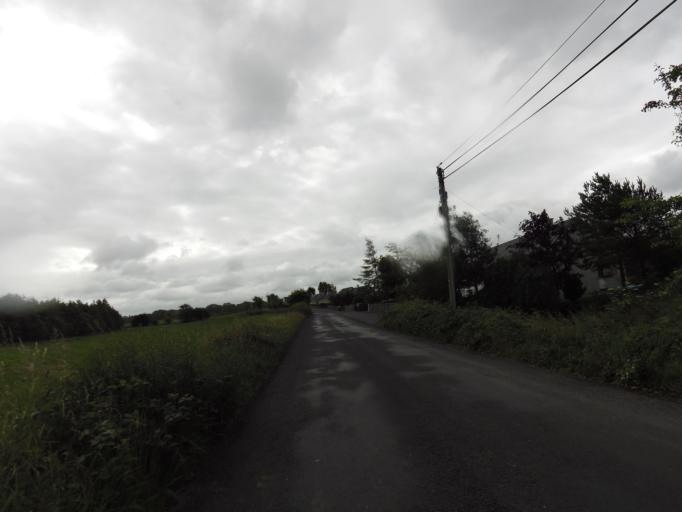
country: IE
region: Connaught
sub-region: County Galway
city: Athenry
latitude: 53.2885
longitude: -8.6930
